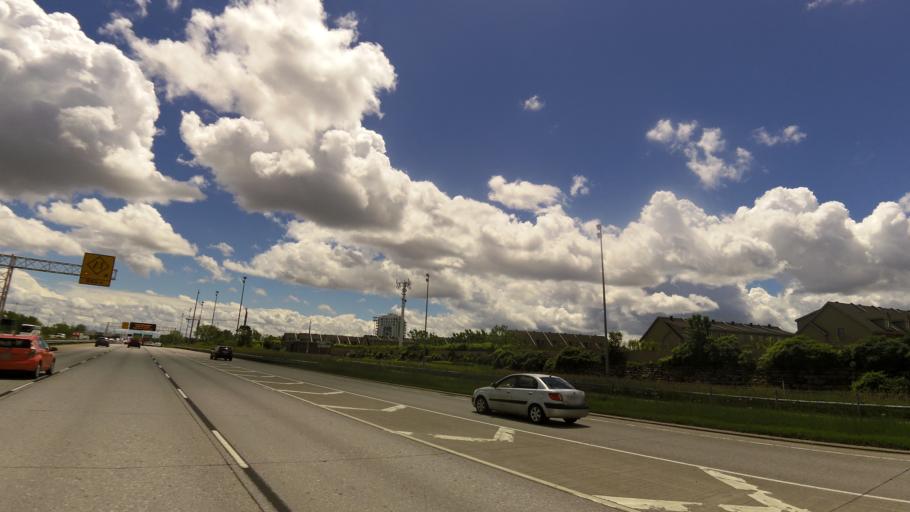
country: CA
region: Quebec
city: Dollard-Des Ormeaux
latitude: 45.5199
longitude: -73.7734
